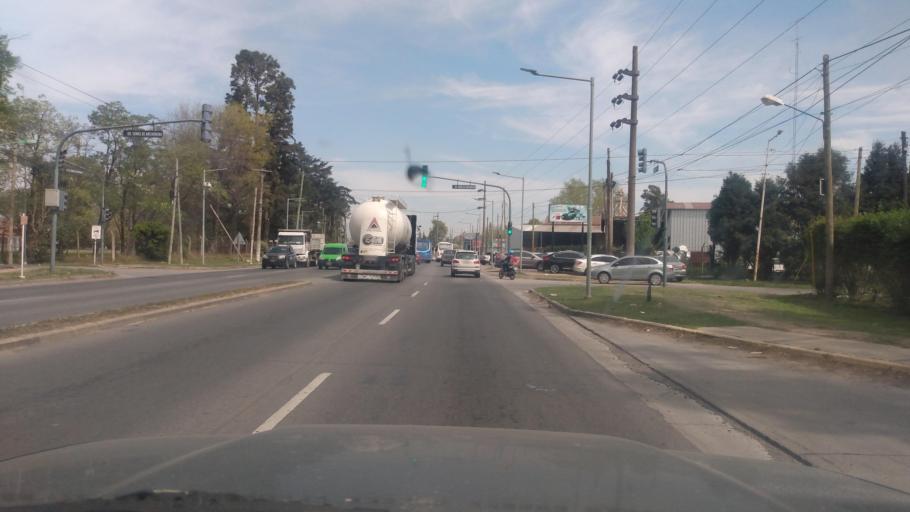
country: AR
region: Buenos Aires
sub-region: Partido de Pilar
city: Pilar
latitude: -34.4427
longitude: -58.9000
